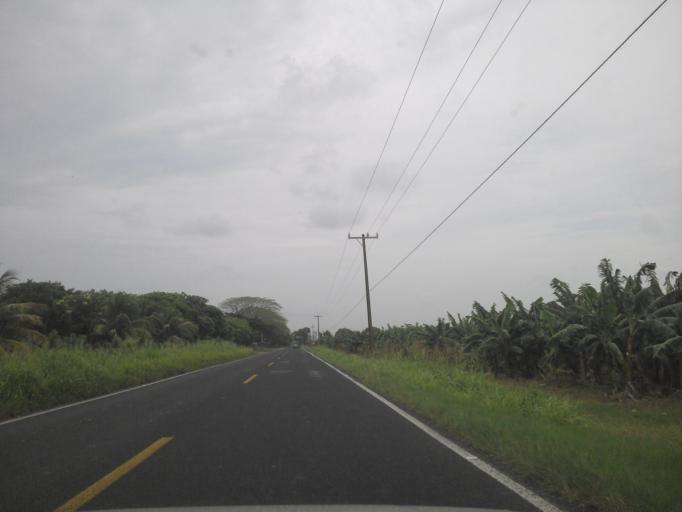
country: MX
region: Veracruz
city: Nautla
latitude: 20.2218
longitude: -96.7863
